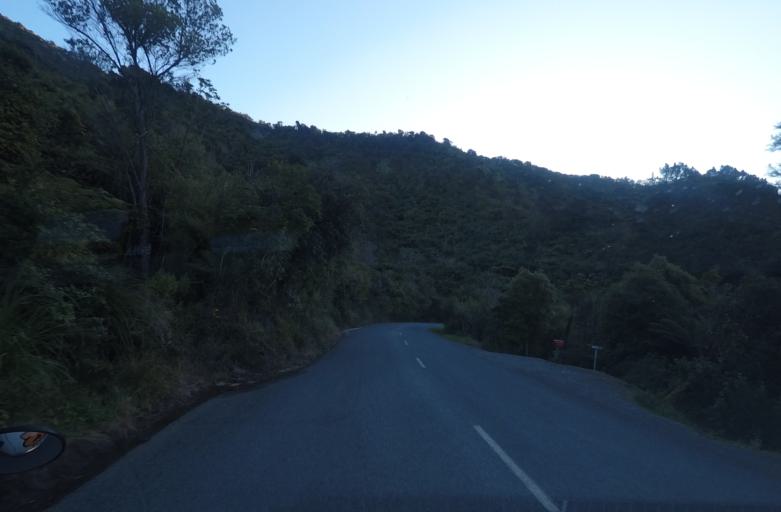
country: NZ
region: Marlborough
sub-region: Marlborough District
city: Picton
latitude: -41.2736
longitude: 173.9586
